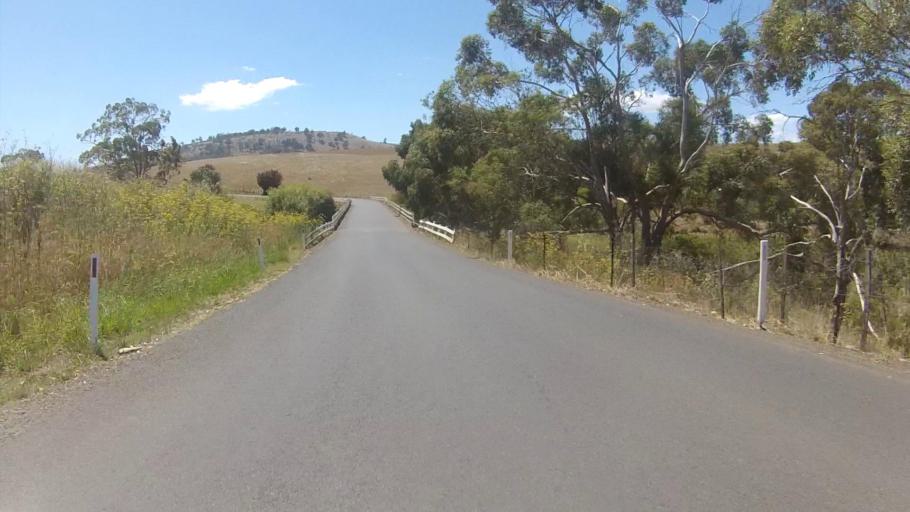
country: AU
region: Tasmania
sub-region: Sorell
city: Sorell
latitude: -42.7722
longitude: 147.5946
